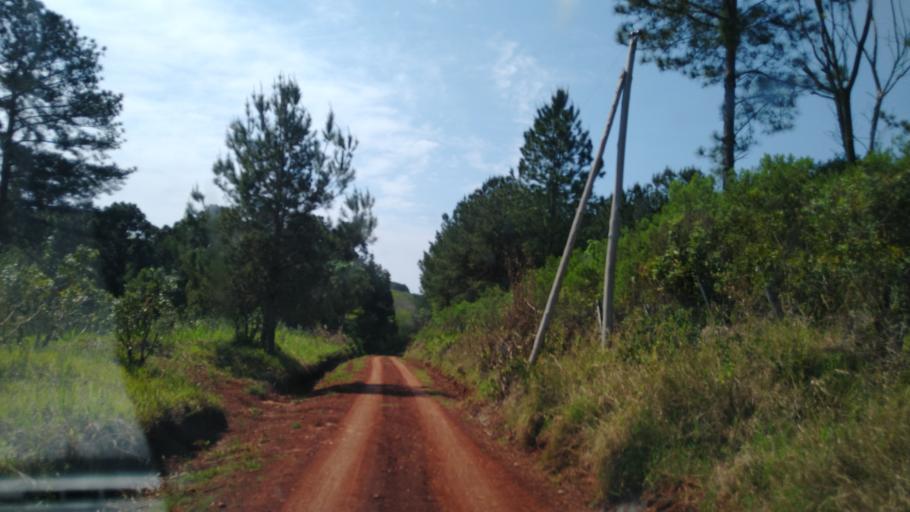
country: AR
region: Misiones
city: Capiovi
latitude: -26.9438
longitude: -55.0525
